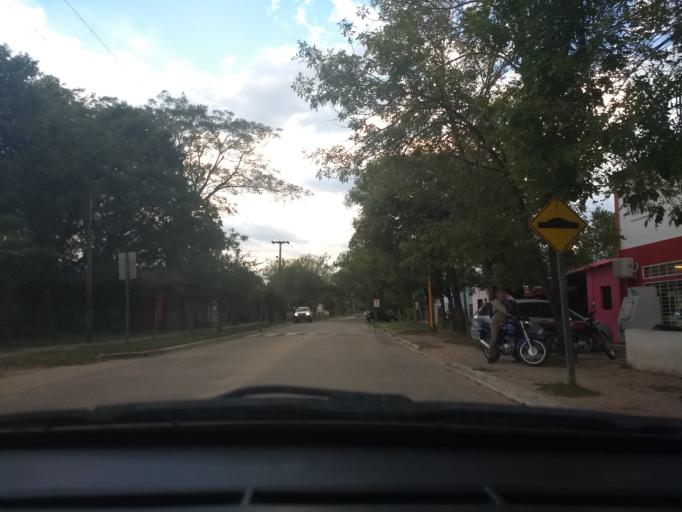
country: AR
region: Corrientes
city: Riachuelo
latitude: -27.5819
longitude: -58.7449
